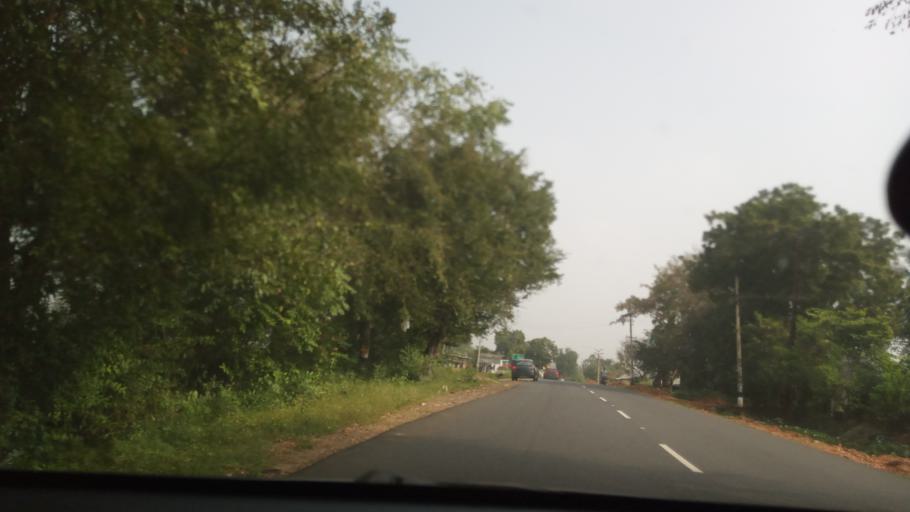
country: IN
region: Tamil Nadu
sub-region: Erode
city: Punjai Puliyampatti
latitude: 11.3261
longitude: 77.1489
